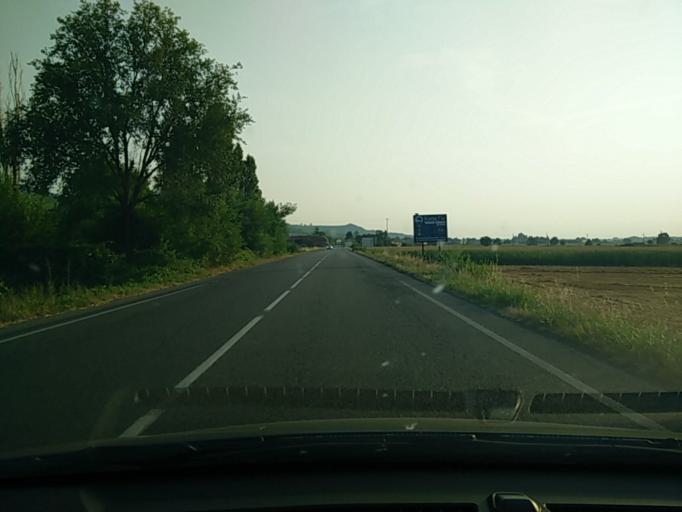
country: IT
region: Lombardy
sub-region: Provincia di Pavia
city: Redavalle
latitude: 45.0442
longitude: 9.2197
